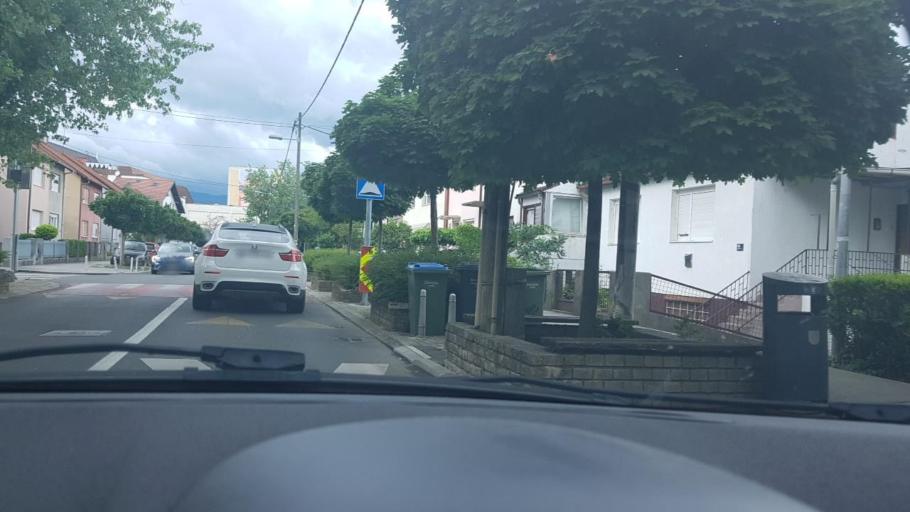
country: HR
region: Grad Zagreb
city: Zagreb
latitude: 45.8084
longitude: 16.0174
